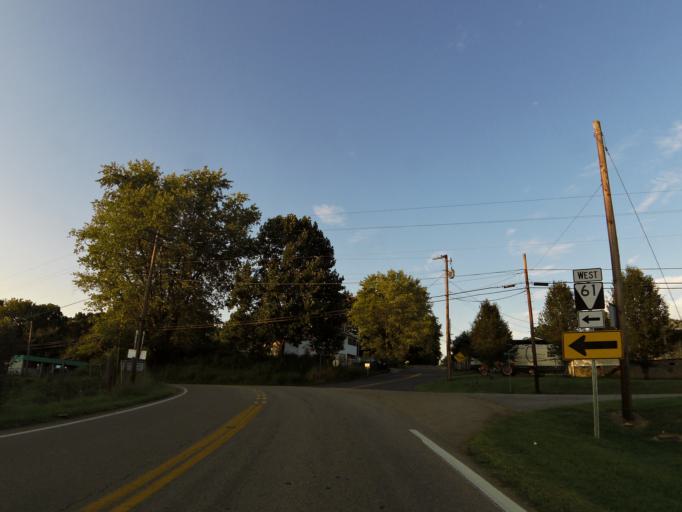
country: US
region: Tennessee
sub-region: Union County
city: Luttrell
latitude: 36.1996
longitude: -83.7428
